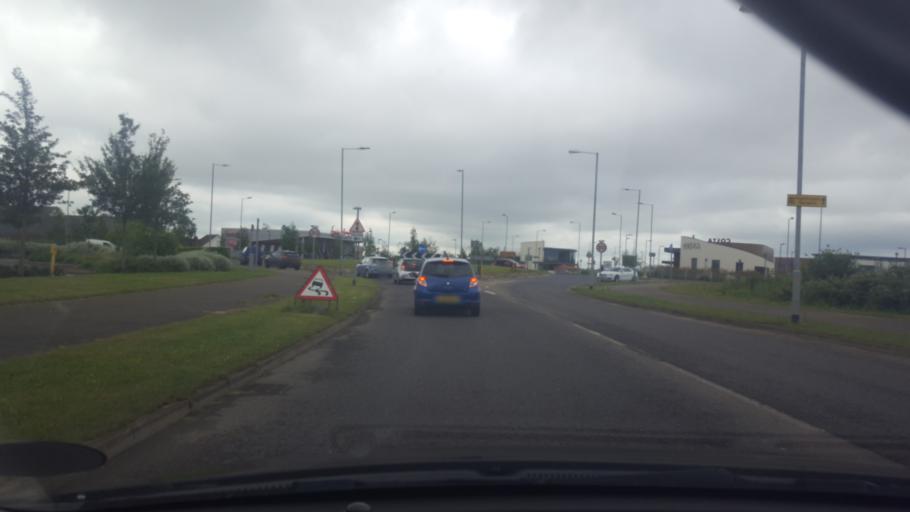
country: GB
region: England
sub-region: Essex
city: Eight Ash Green
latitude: 51.8863
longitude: 0.8269
